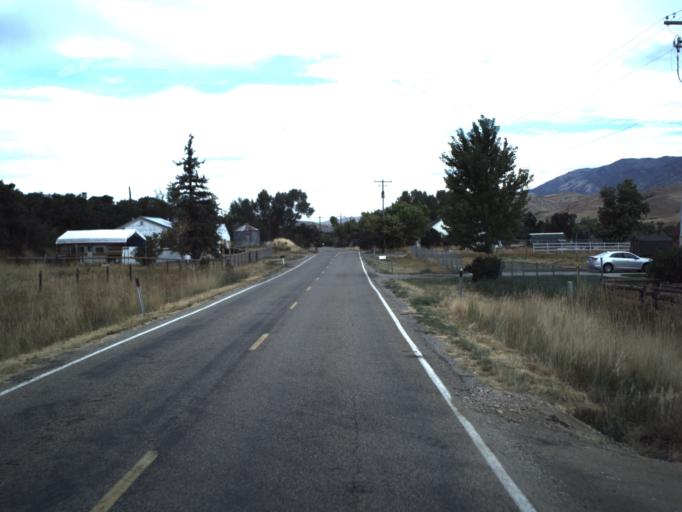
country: US
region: Utah
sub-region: Morgan County
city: Morgan
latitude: 40.9589
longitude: -111.6674
